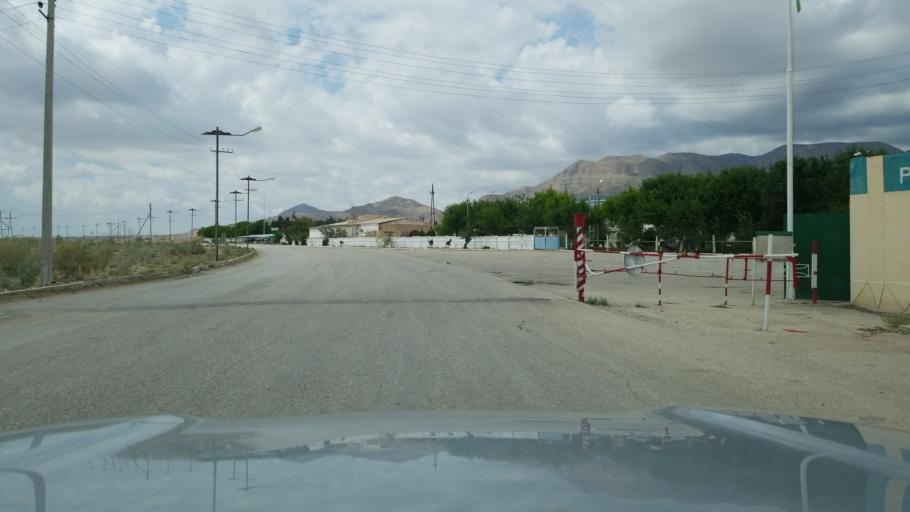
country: TM
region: Balkan
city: Balkanabat
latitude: 39.4787
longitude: 54.4594
